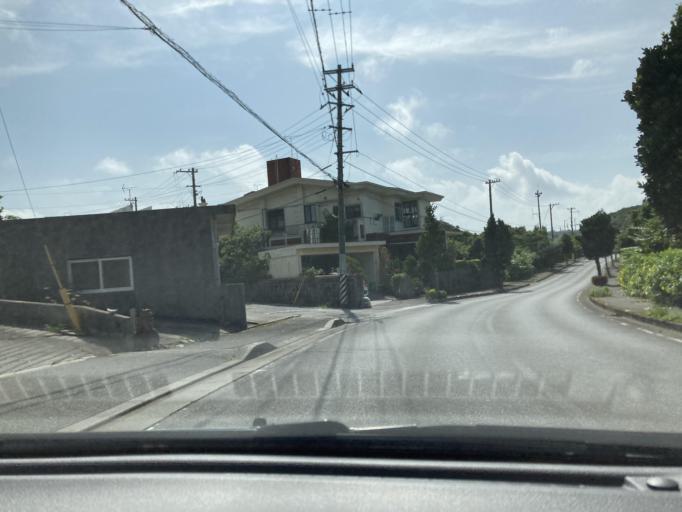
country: JP
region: Okinawa
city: Chatan
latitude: 26.2883
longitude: 127.8033
